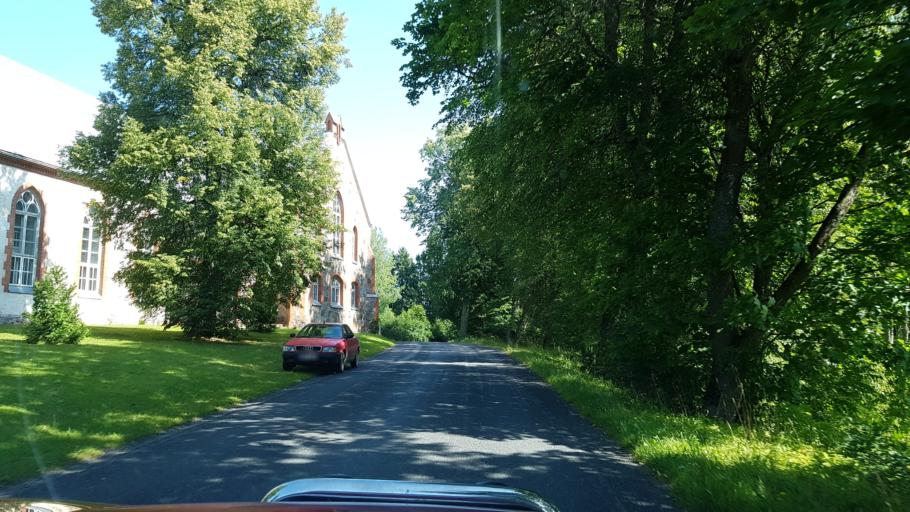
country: EE
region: Vorumaa
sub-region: Voru linn
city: Voru
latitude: 57.7466
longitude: 27.2663
